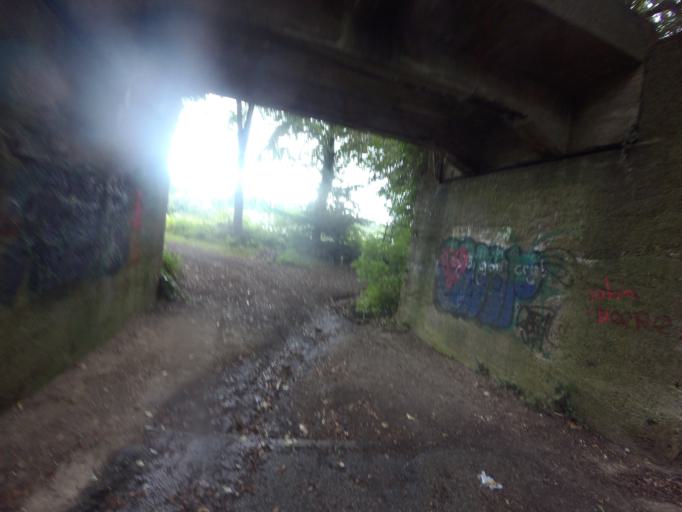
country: NL
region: Limburg
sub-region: Eijsden-Margraten
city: Margraten
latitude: 50.8052
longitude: 5.8658
